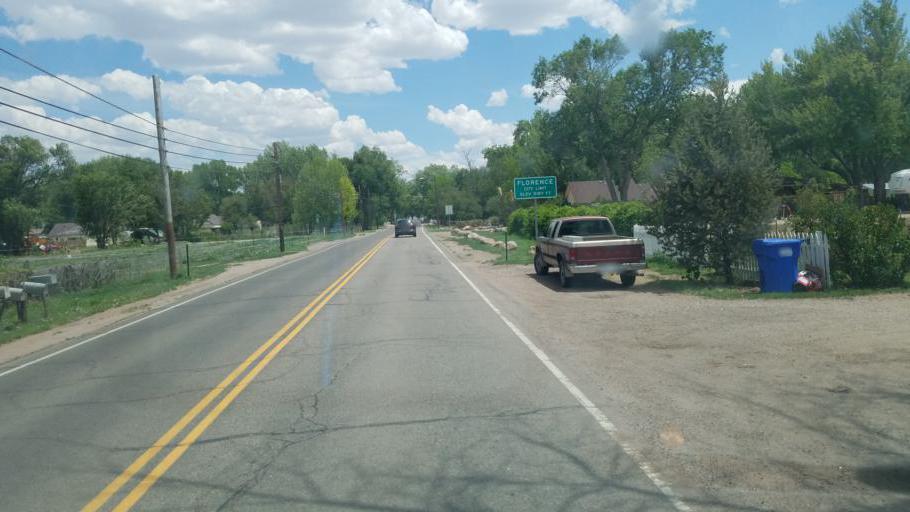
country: US
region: Colorado
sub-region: Fremont County
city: Florence
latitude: 38.3977
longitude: -105.1301
